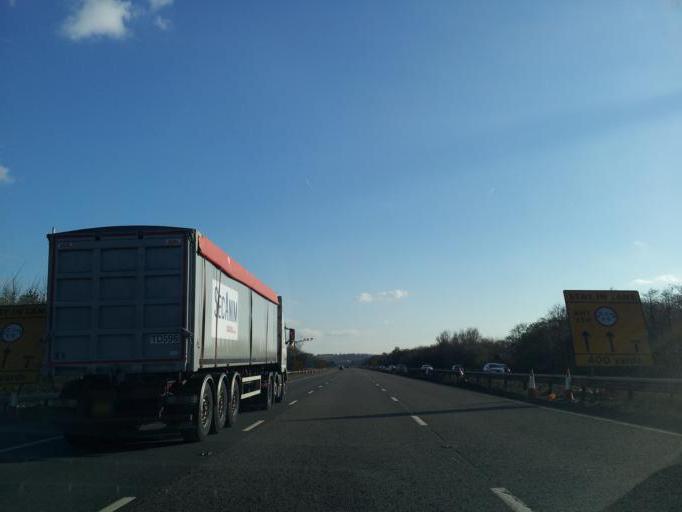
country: GB
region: England
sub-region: Devon
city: Cullompton
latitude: 50.8728
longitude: -3.3820
